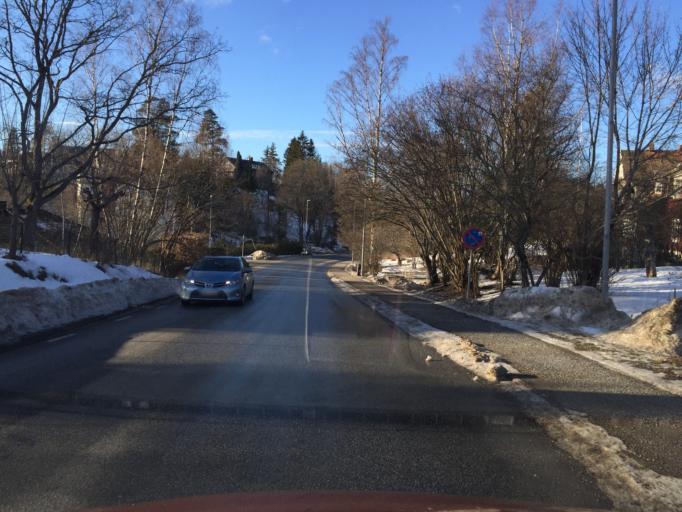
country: SE
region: Stockholm
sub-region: Salems Kommun
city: Ronninge
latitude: 59.1985
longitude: 17.7416
